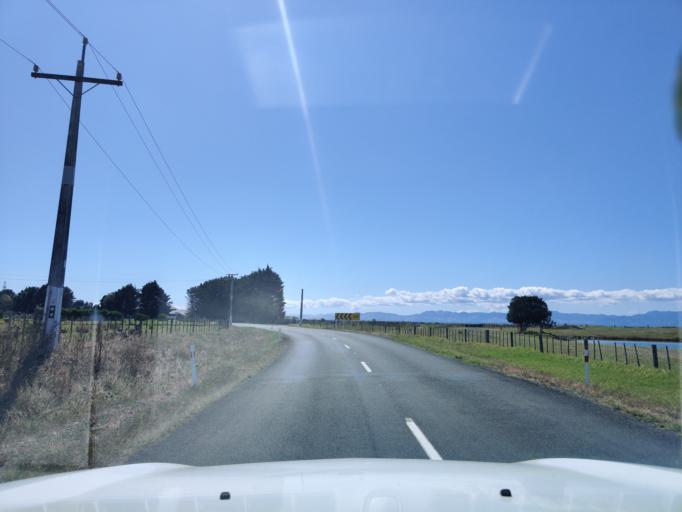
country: NZ
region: Waikato
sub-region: Thames-Coromandel District
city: Thames
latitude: -37.0556
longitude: 175.3015
